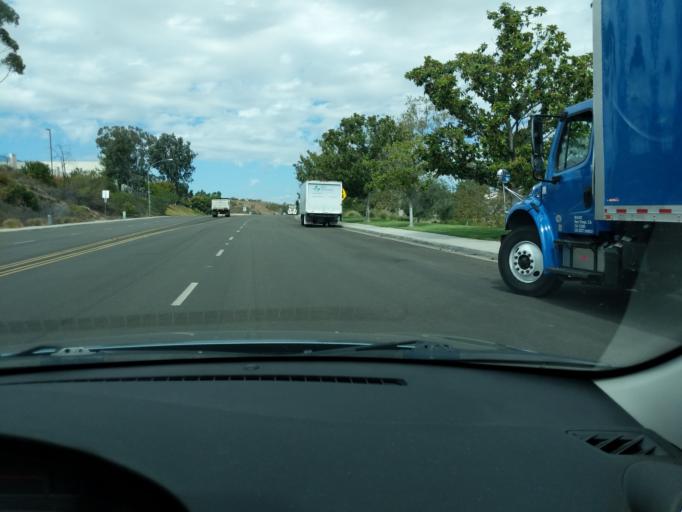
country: US
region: California
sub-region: San Diego County
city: San Diego
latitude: 32.8062
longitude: -117.1223
